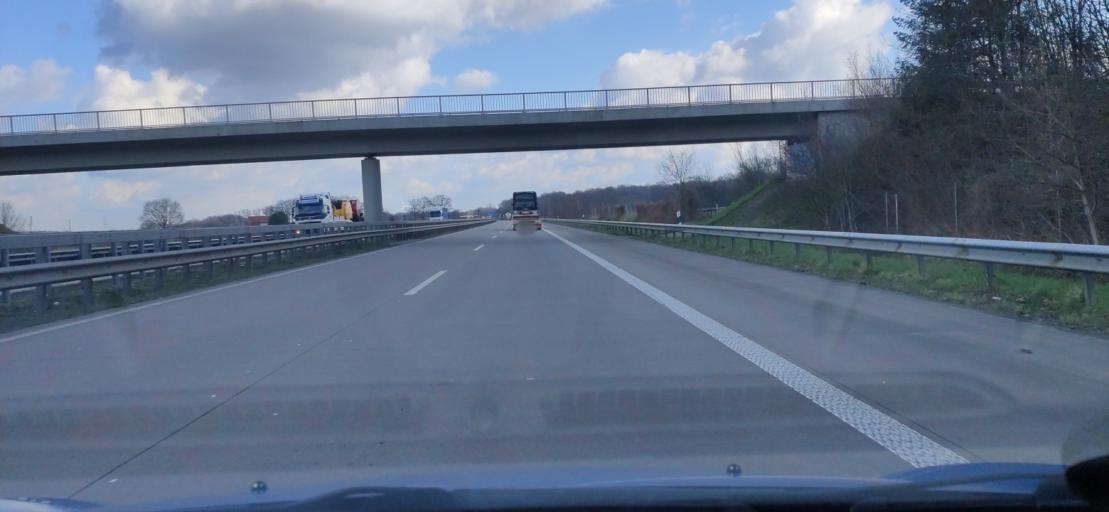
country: DE
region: Lower Saxony
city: Isterberg
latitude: 52.3368
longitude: 7.1299
